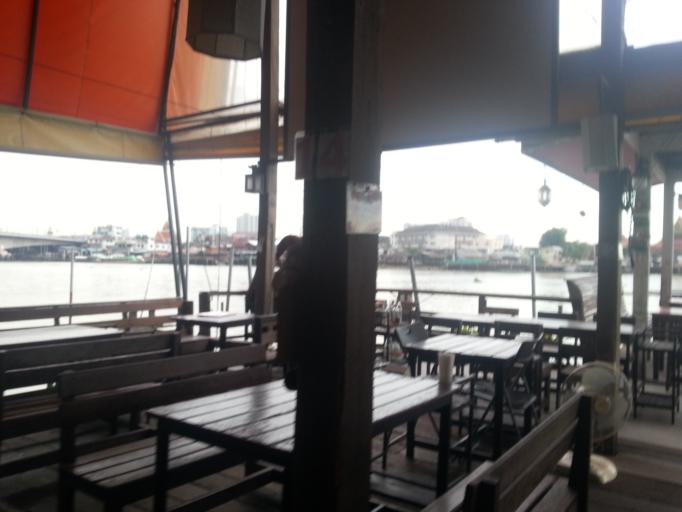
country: TH
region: Nonthaburi
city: Pak Kret
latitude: 13.9159
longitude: 100.4915
